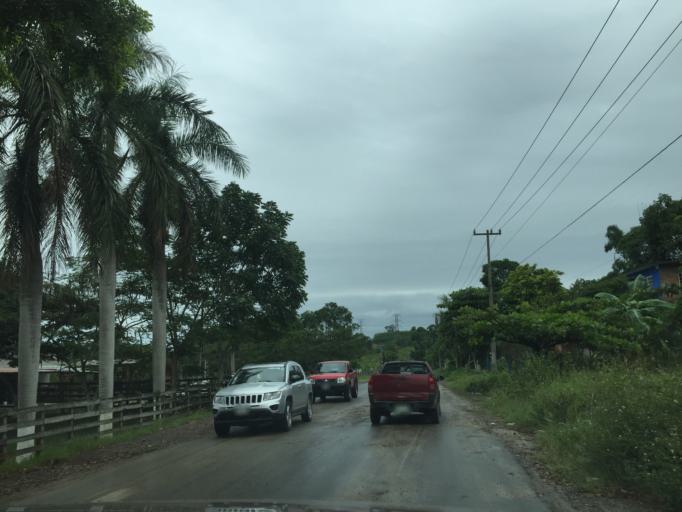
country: MX
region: Veracruz
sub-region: Papantla
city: El Chote
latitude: 20.4409
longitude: -97.4029
